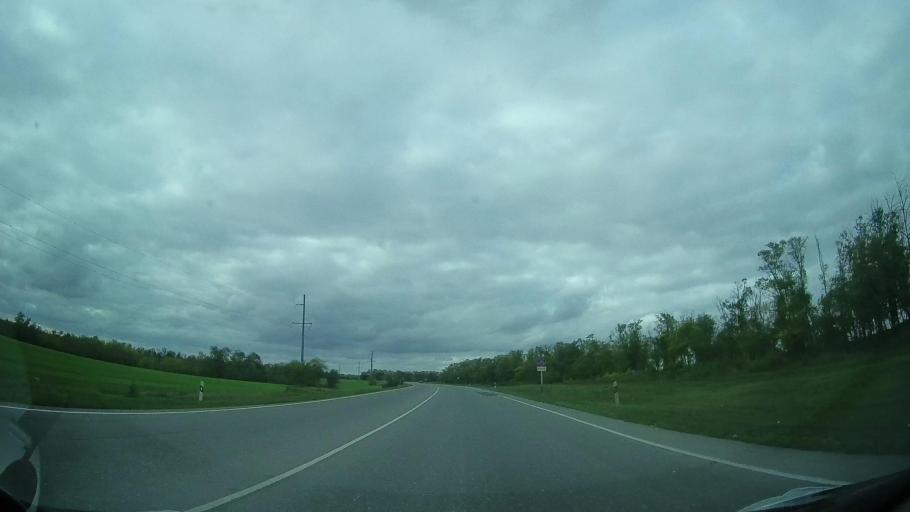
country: RU
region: Rostov
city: Mechetinskaya
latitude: 46.7846
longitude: 40.4105
